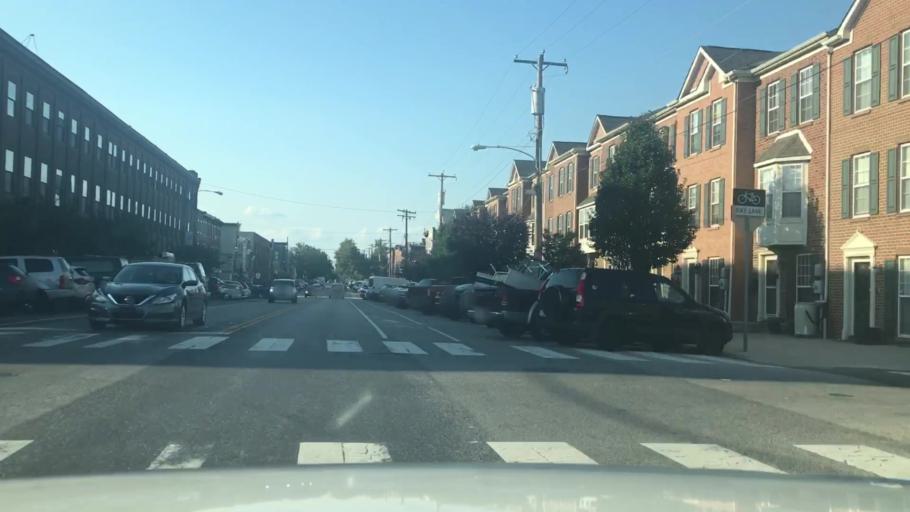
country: US
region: Pennsylvania
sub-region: Philadelphia County
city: Philadelphia
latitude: 39.9771
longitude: -75.1238
